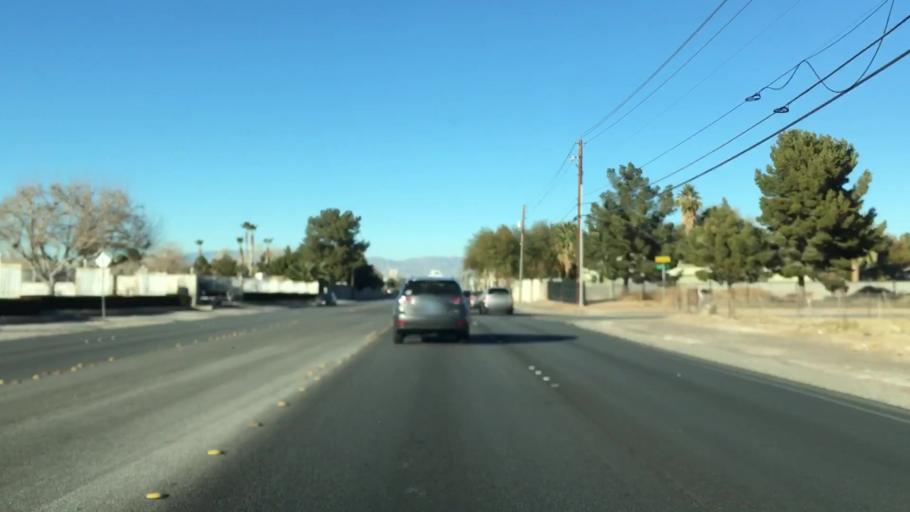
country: US
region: Nevada
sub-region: Clark County
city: Whitney
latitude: 36.0684
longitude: -115.1006
